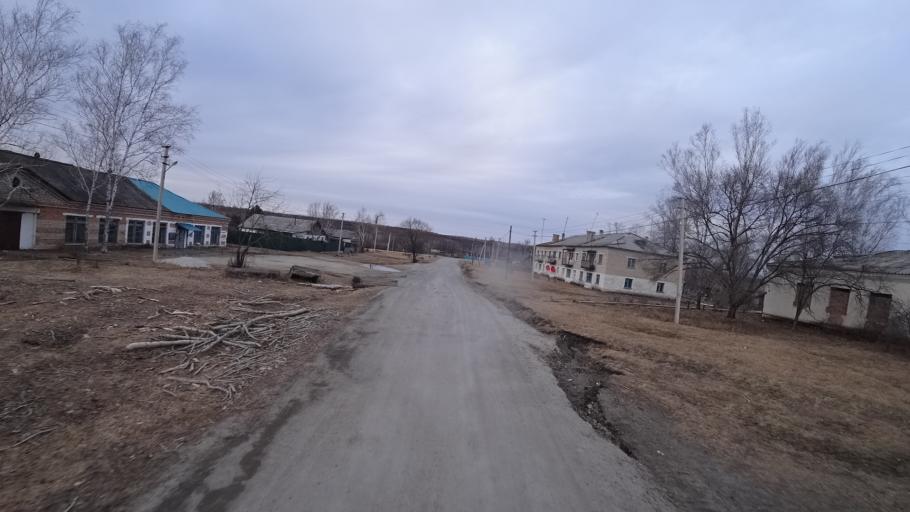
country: RU
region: Amur
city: Bureya
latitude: 50.0187
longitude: 129.7684
